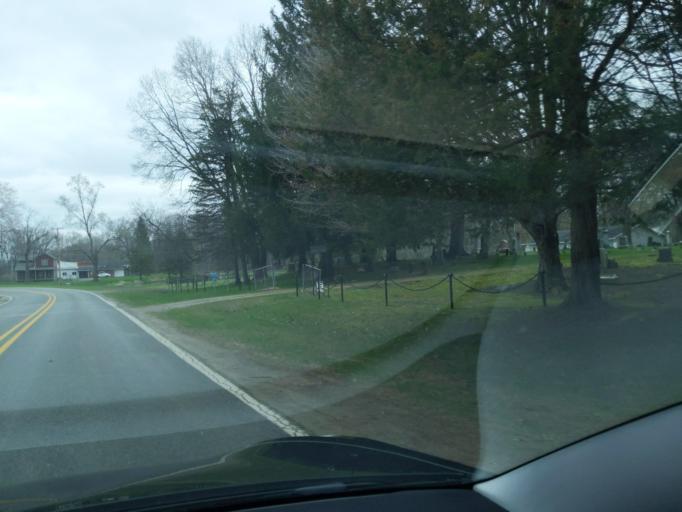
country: US
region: Michigan
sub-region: Ingham County
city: Stockbridge
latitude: 42.4408
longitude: -84.0967
